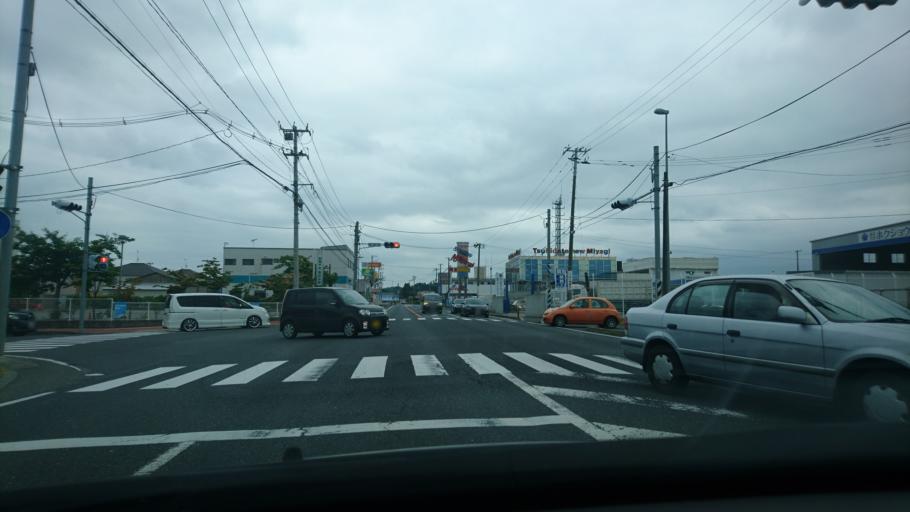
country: JP
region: Miyagi
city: Furukawa
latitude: 38.7466
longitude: 141.0147
